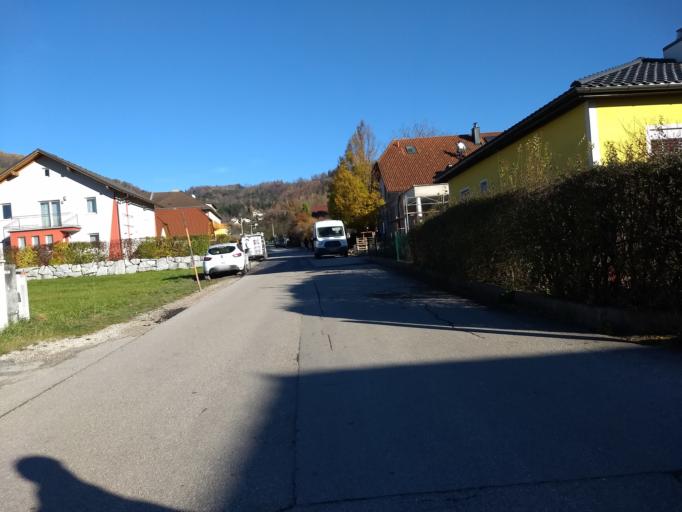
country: AT
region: Upper Austria
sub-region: Politischer Bezirk Kirchdorf an der Krems
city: Micheldorf in Oberoesterreich
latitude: 47.8936
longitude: 14.1318
